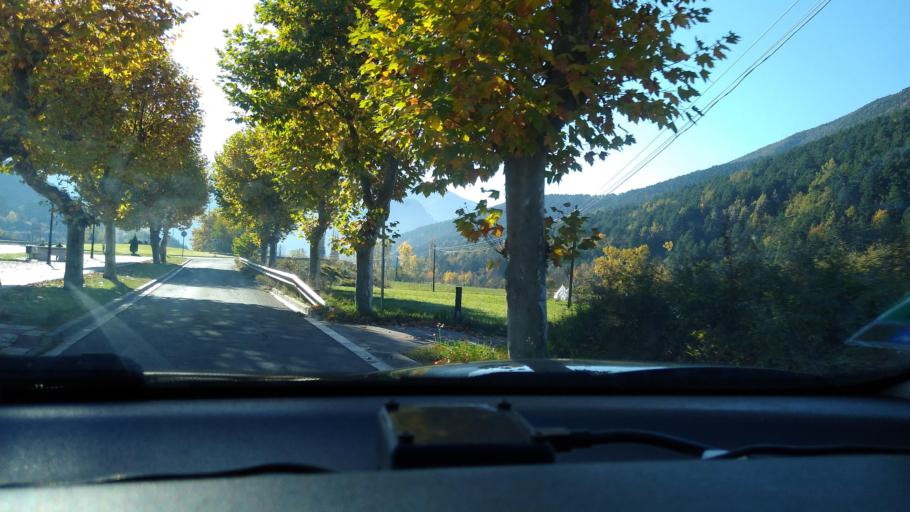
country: ES
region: Catalonia
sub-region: Provincia de Barcelona
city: Baga
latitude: 42.2476
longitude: 1.8676
